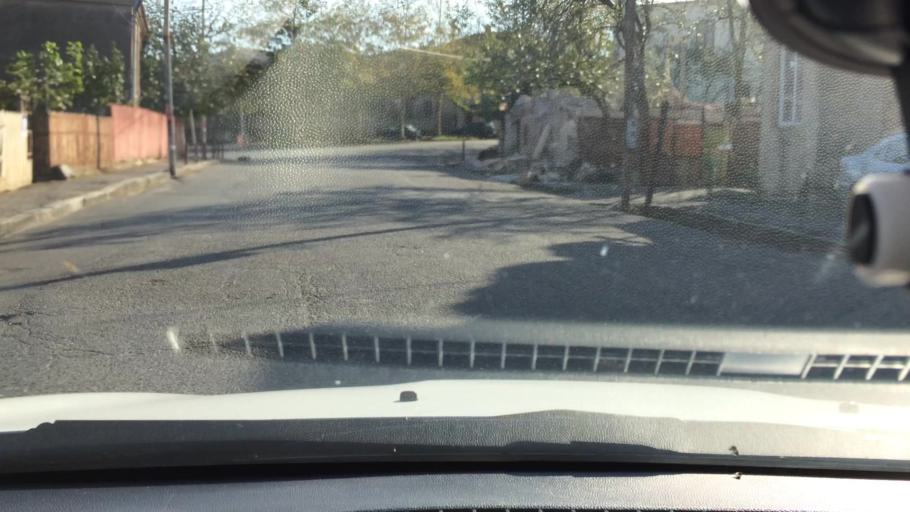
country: GE
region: Imereti
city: Kutaisi
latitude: 42.2692
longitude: 42.7140
